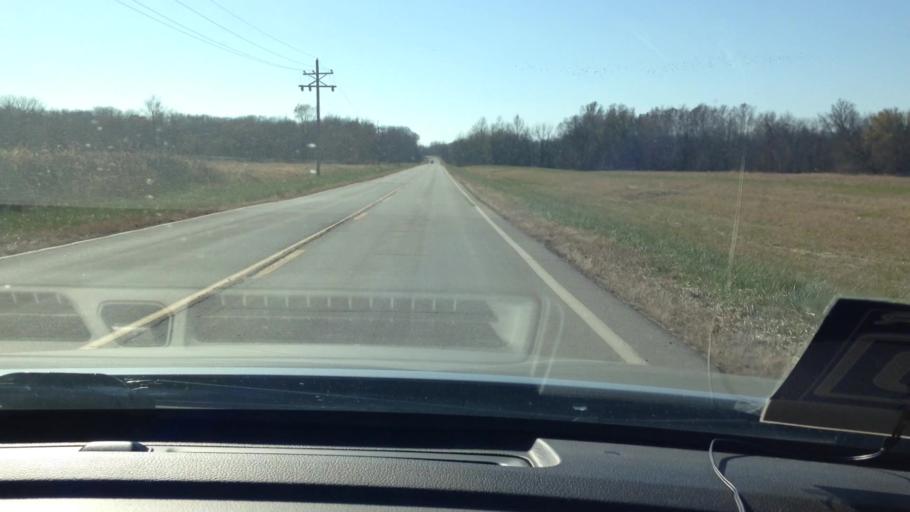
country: US
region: Missouri
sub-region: Platte County
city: Platte City
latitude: 39.4870
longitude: -94.8056
